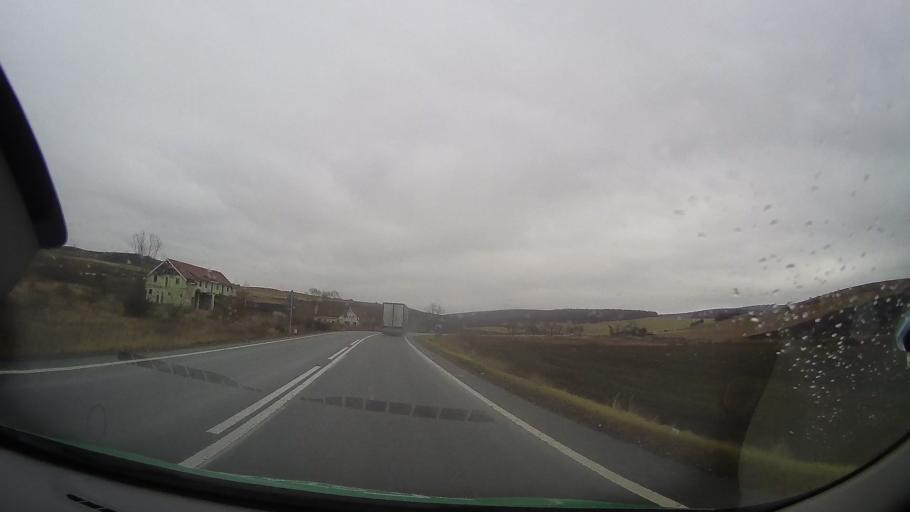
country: RO
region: Mures
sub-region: Comuna Lunca
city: Lunca
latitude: 46.8700
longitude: 24.5527
